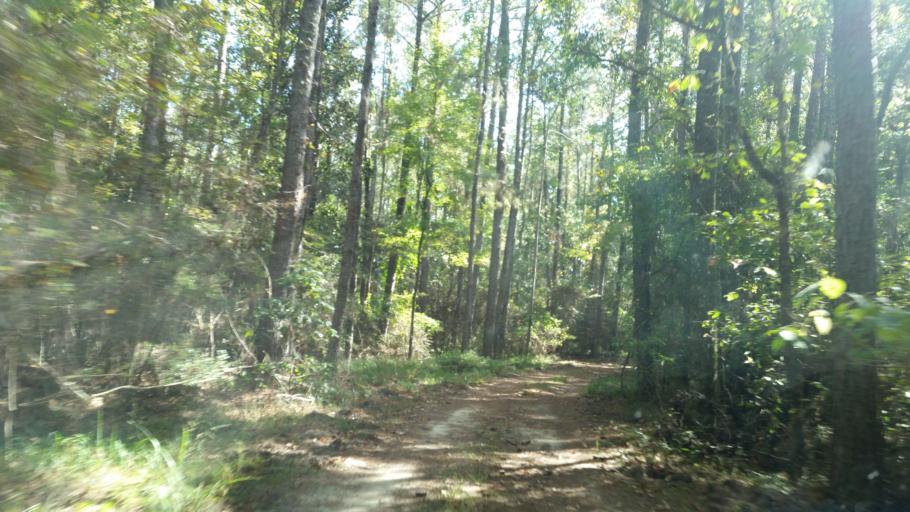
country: US
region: Alabama
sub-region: Baldwin County
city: Spanish Fort
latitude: 30.7382
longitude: -87.9194
